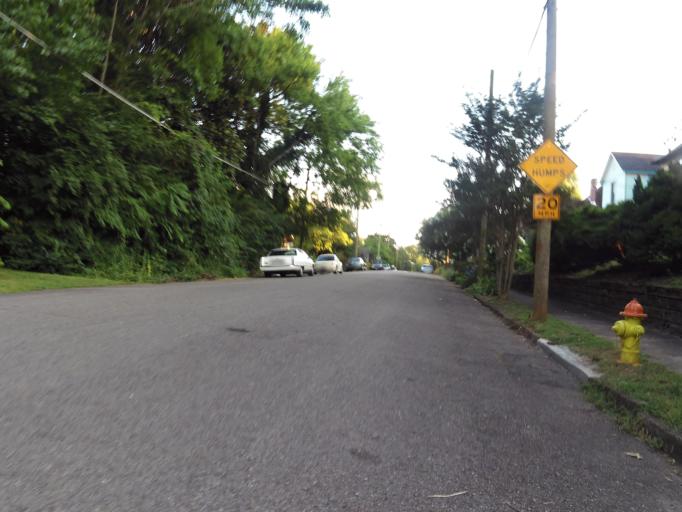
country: US
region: Tennessee
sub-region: Knox County
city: Knoxville
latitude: 35.9890
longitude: -83.9234
